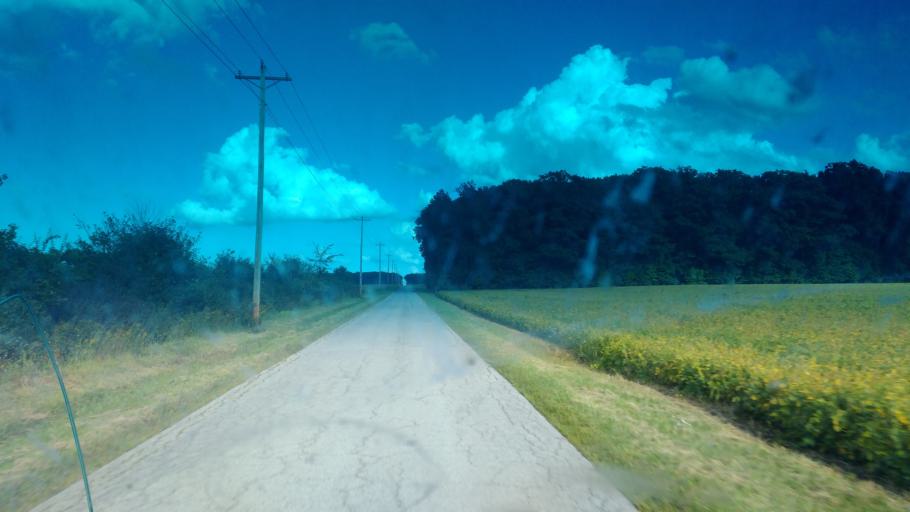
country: US
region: Ohio
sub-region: Hancock County
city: Arlington
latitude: 40.9360
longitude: -83.7389
